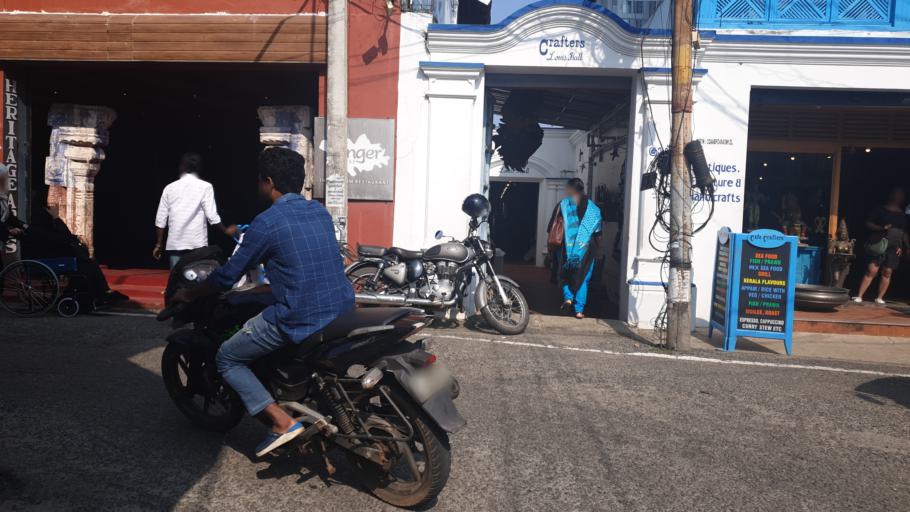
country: IN
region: Kerala
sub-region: Ernakulam
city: Cochin
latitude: 9.9565
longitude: 76.2603
